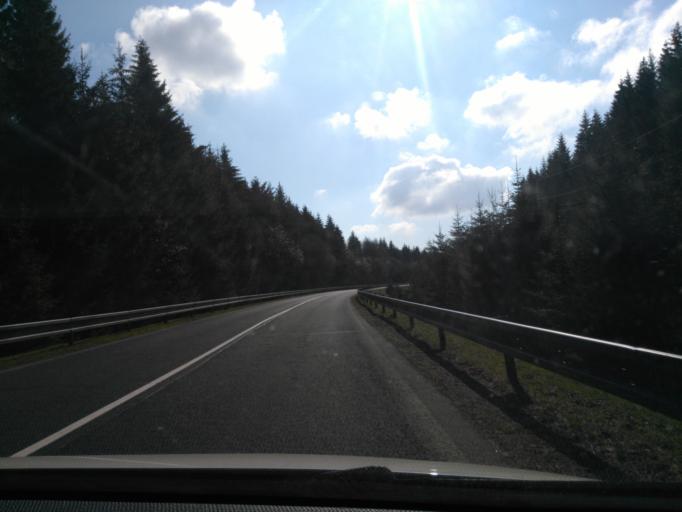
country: DE
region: Saxony
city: Johstadt
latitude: 50.4733
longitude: 13.1174
